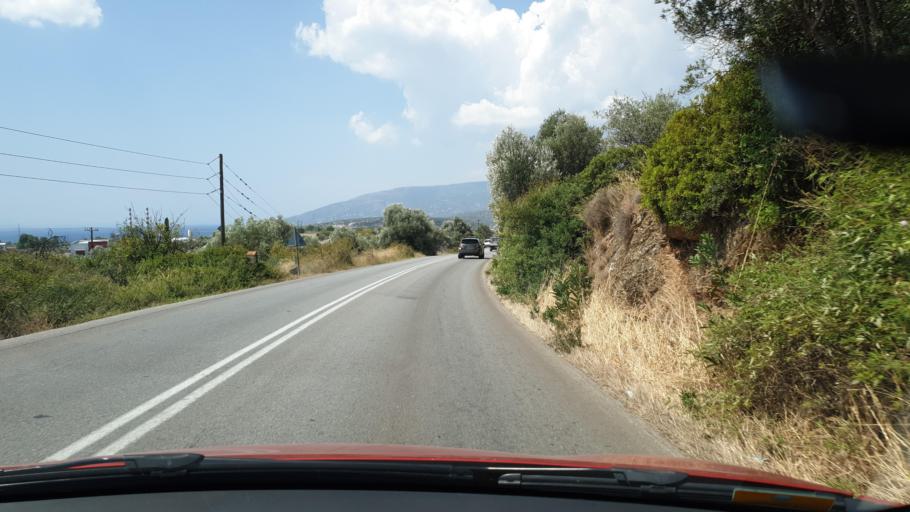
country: GR
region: Central Greece
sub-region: Nomos Evvoias
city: Aliveri
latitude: 38.3939
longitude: 24.0755
